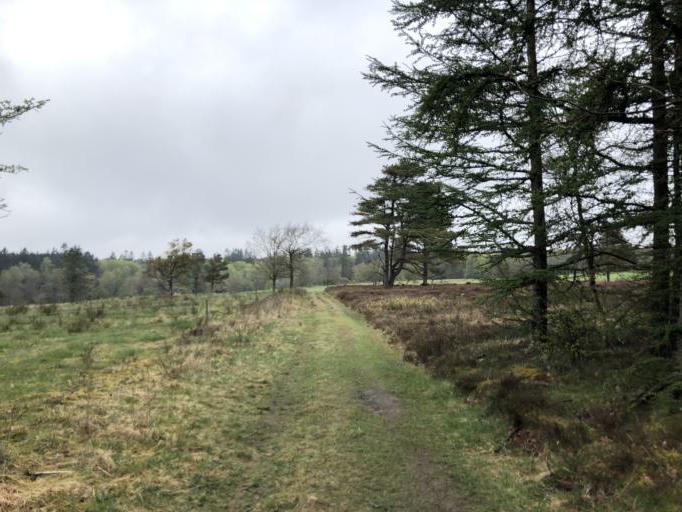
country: DK
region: Central Jutland
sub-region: Lemvig Kommune
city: Lemvig
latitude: 56.4815
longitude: 8.3609
